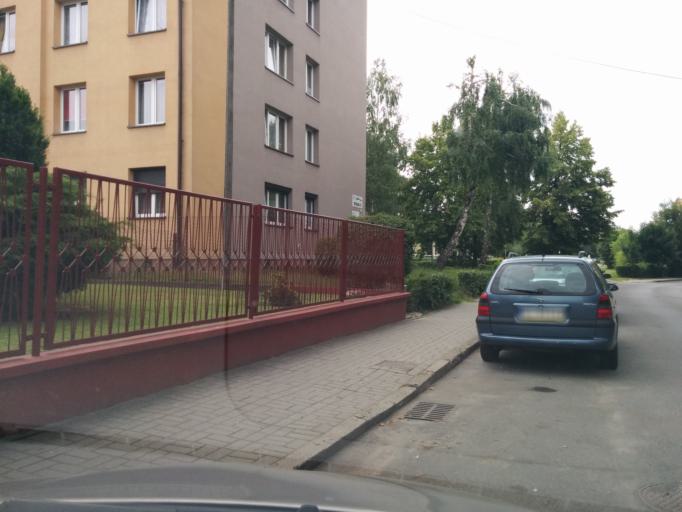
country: PL
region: Silesian Voivodeship
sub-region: Ruda Slaska
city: Ruda Slaska
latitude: 50.2408
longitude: 18.8352
